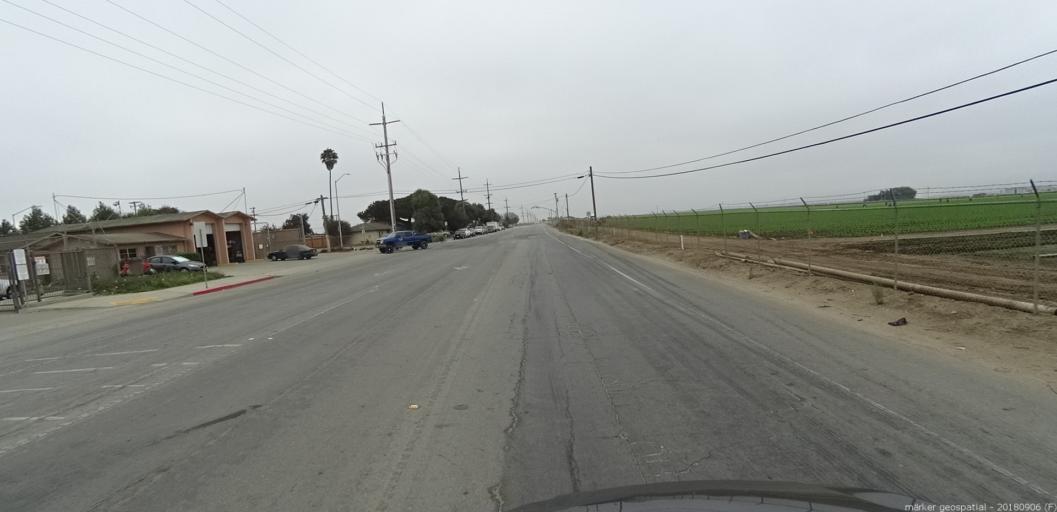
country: US
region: California
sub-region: Monterey County
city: Salinas
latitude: 36.6729
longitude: -121.6012
